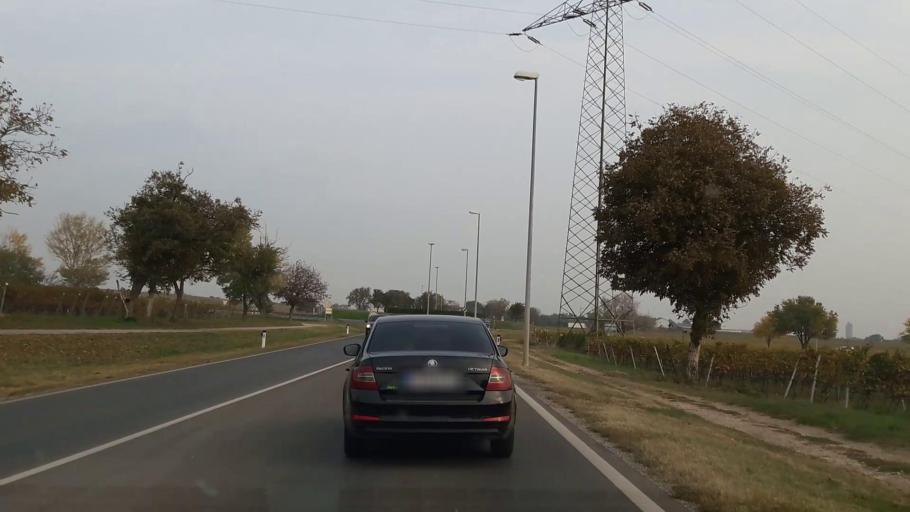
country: AT
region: Burgenland
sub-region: Politischer Bezirk Neusiedl am See
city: Weiden am See
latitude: 47.9131
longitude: 16.8865
